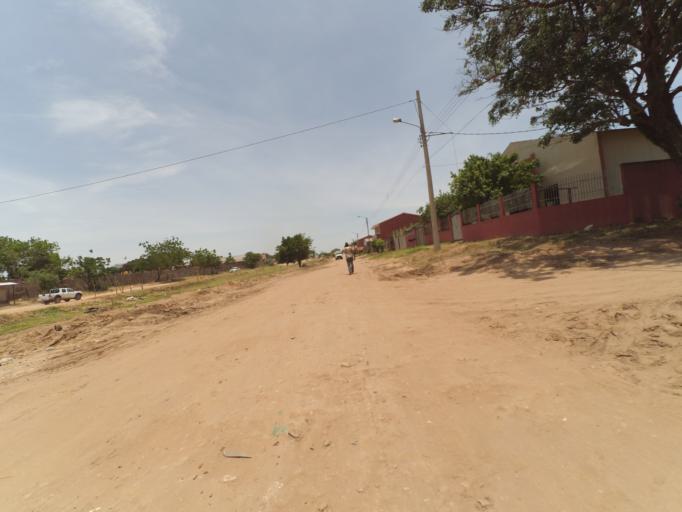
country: BO
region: Santa Cruz
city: Santa Cruz de la Sierra
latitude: -17.8298
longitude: -63.2428
